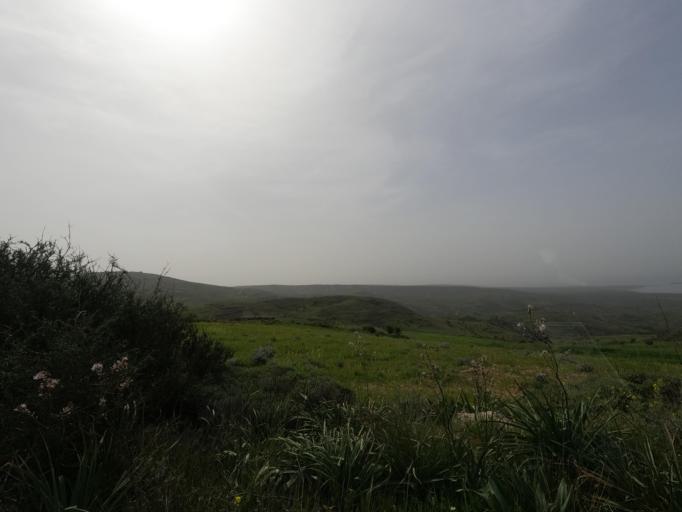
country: CY
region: Pafos
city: Polis
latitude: 34.9763
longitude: 32.3514
